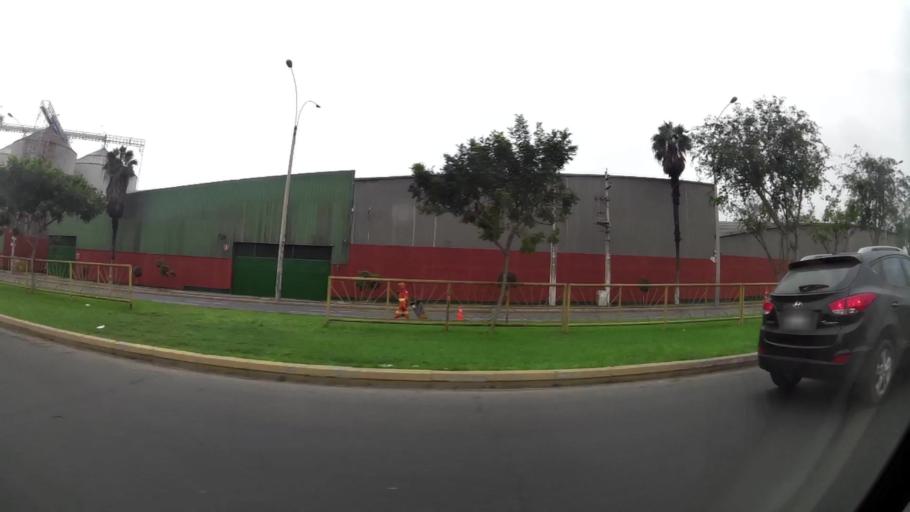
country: PE
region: Lima
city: Lima
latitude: -12.0582
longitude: -77.0706
